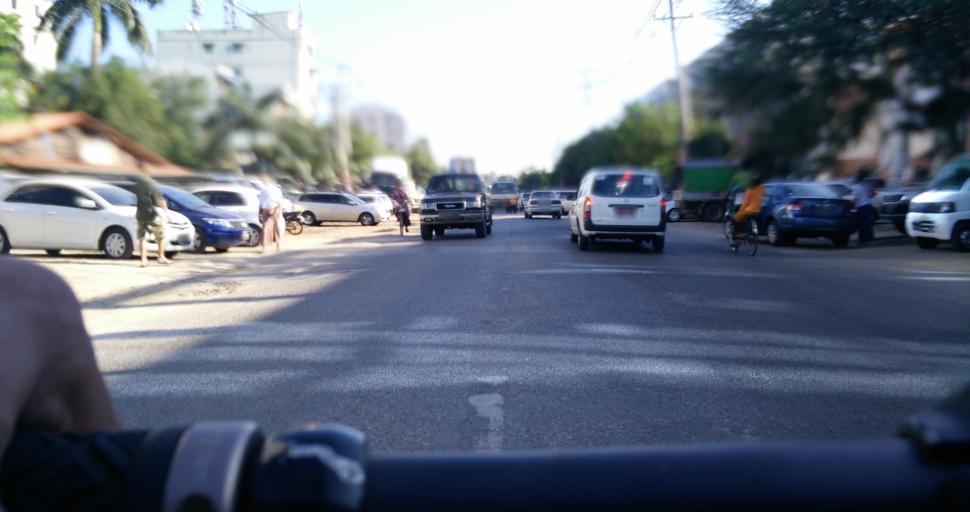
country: MM
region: Yangon
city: Yangon
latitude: 16.8436
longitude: 96.1985
